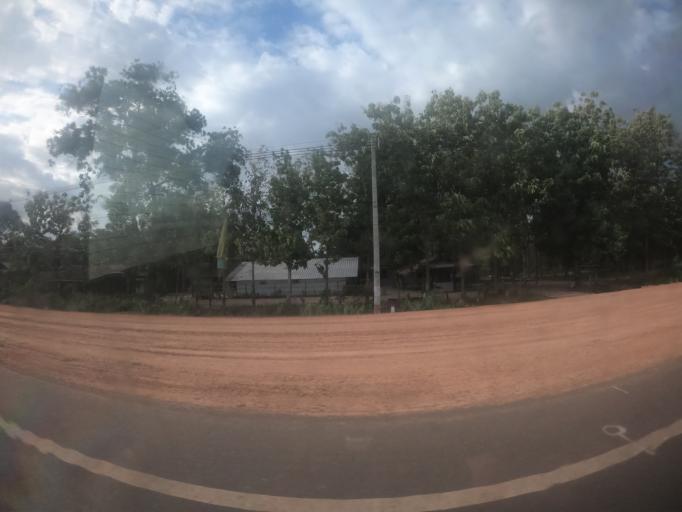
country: TH
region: Surin
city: Kap Choeng
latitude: 14.4732
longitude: 103.6062
